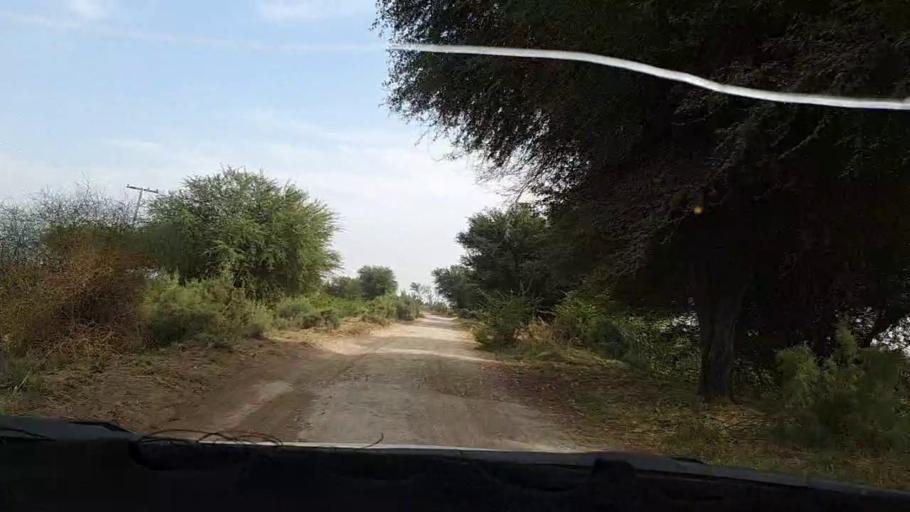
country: PK
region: Sindh
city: Pithoro
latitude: 25.5474
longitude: 69.3296
